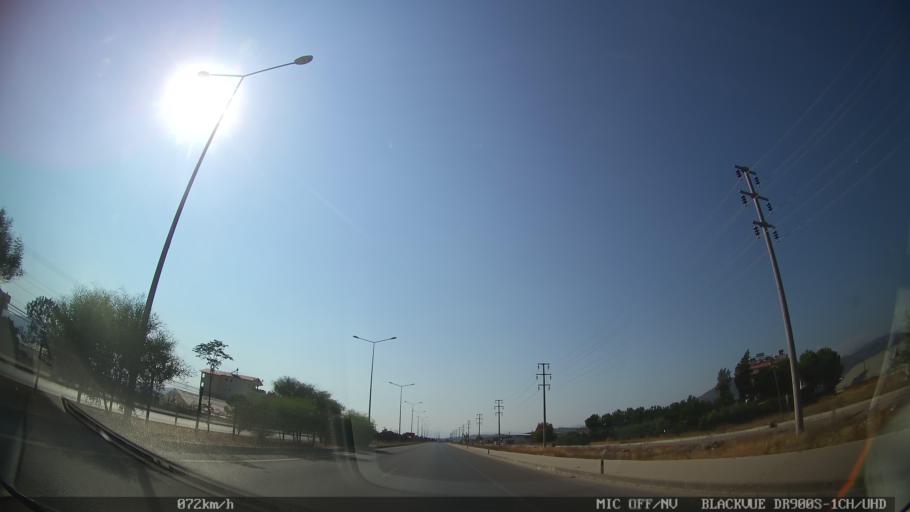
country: TR
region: Mugla
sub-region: Fethiye
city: Fethiye
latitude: 36.6538
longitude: 29.1694
